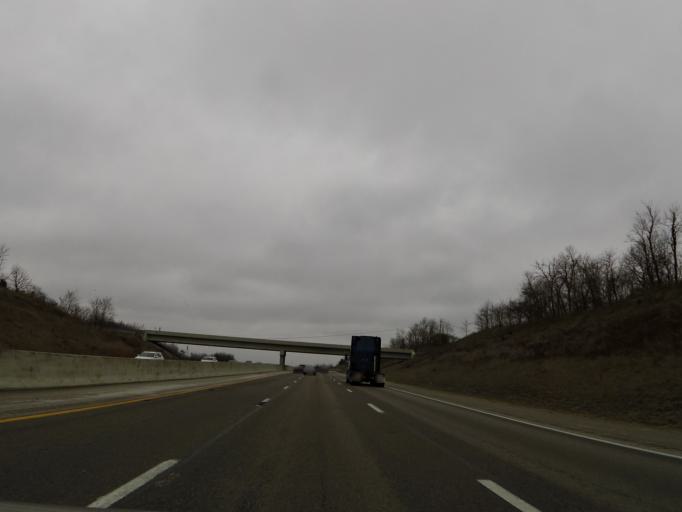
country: US
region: Kentucky
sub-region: Grant County
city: Williamstown
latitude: 38.5980
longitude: -84.5822
